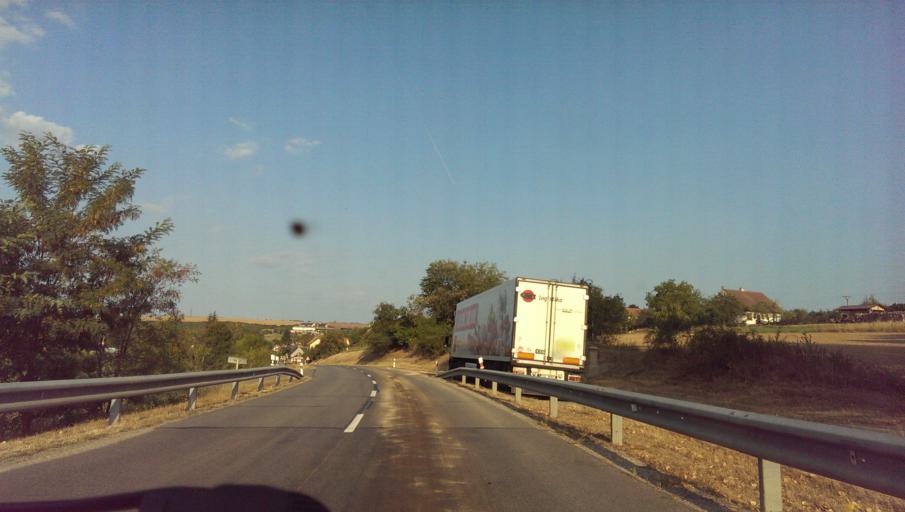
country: CZ
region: South Moravian
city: Zeravice
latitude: 49.0548
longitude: 17.2598
